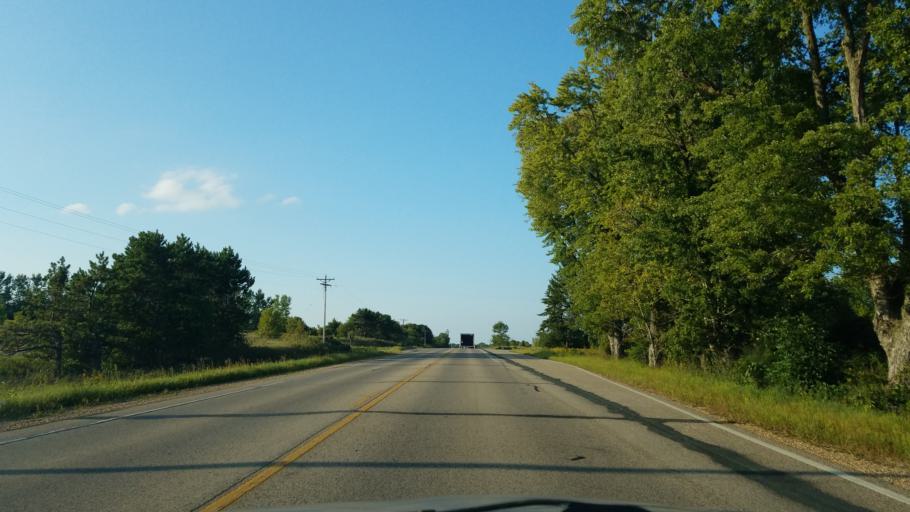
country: US
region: Wisconsin
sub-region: Saint Croix County
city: New Richmond
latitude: 45.0721
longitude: -92.5374
